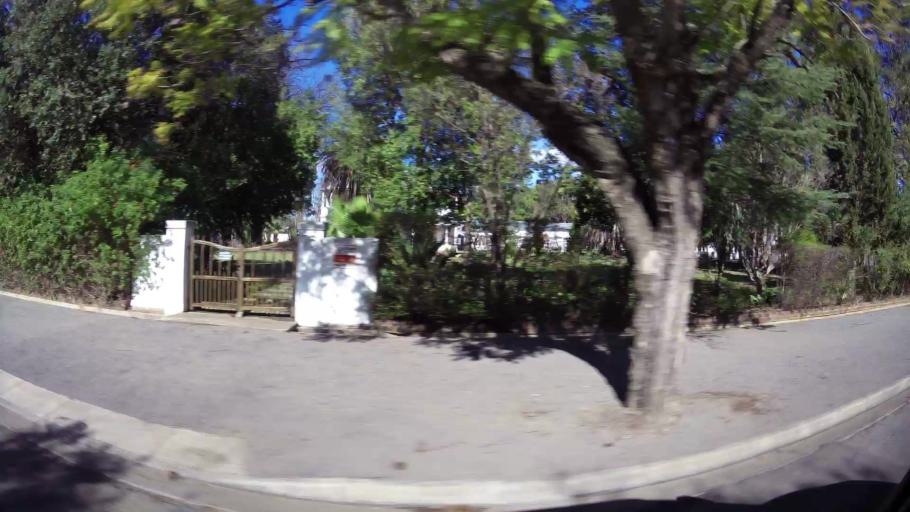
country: ZA
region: Western Cape
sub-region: Cape Winelands District Municipality
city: Ashton
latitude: -33.8000
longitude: 19.8863
